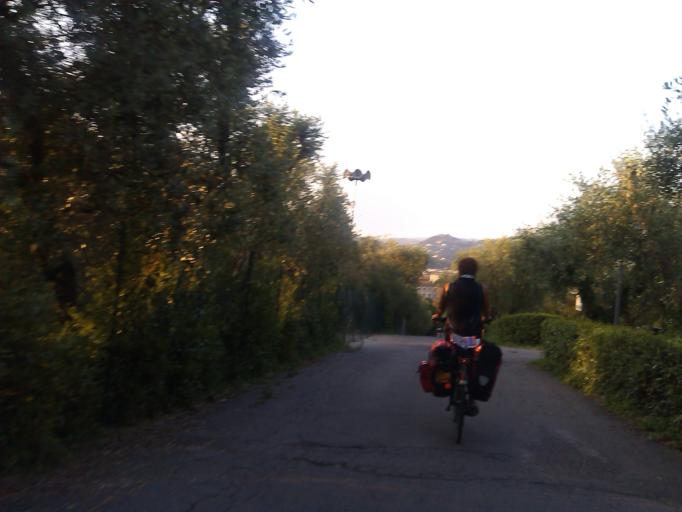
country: IT
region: Tuscany
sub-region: Province of Florence
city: Florence
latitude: 43.7621
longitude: 11.2681
